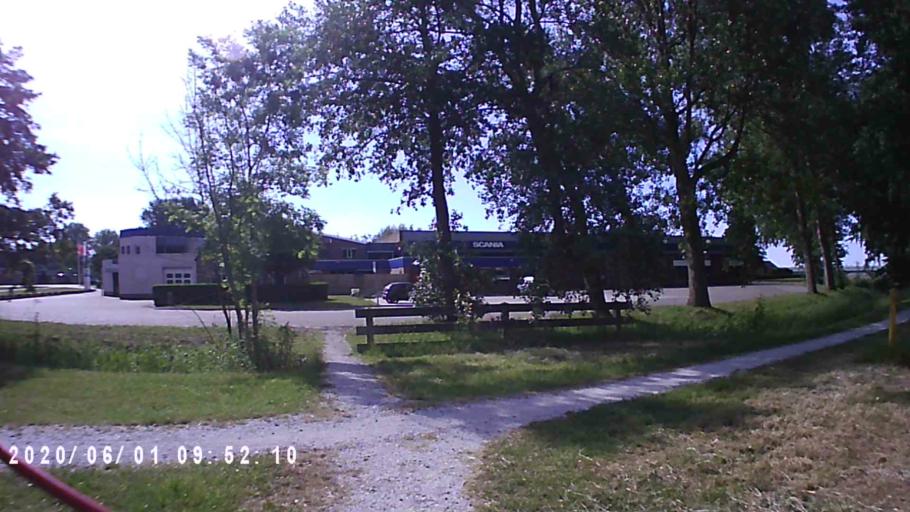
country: NL
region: Friesland
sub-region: Menameradiel
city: Berltsum
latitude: 53.2426
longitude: 5.6597
